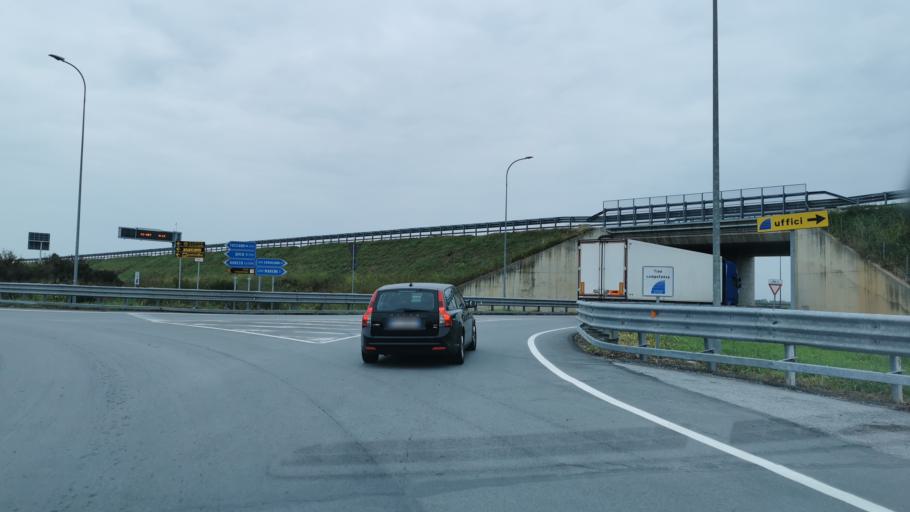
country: IT
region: Piedmont
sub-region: Provincia di Cuneo
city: Roreto
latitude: 44.6642
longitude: 7.8028
